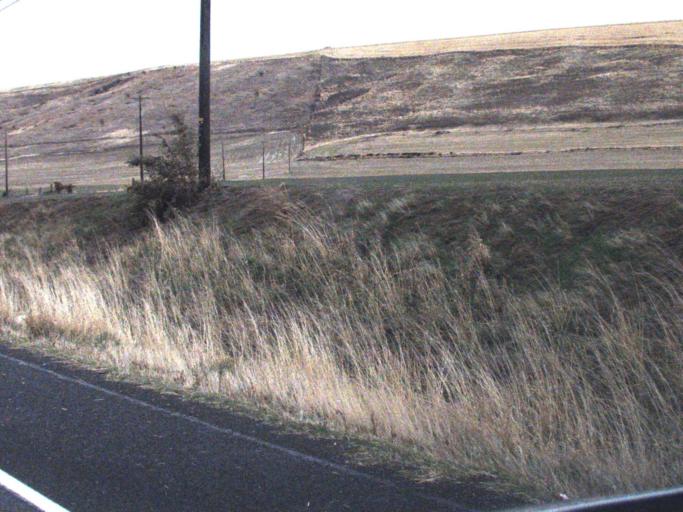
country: US
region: Washington
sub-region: Columbia County
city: Dayton
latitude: 46.3058
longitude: -118.0029
